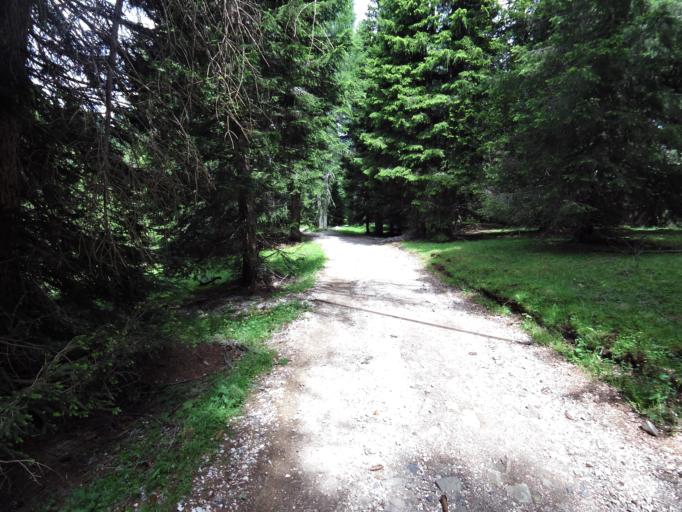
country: IT
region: Trentino-Alto Adige
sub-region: Bolzano
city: Ortisei
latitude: 46.5309
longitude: 11.6469
